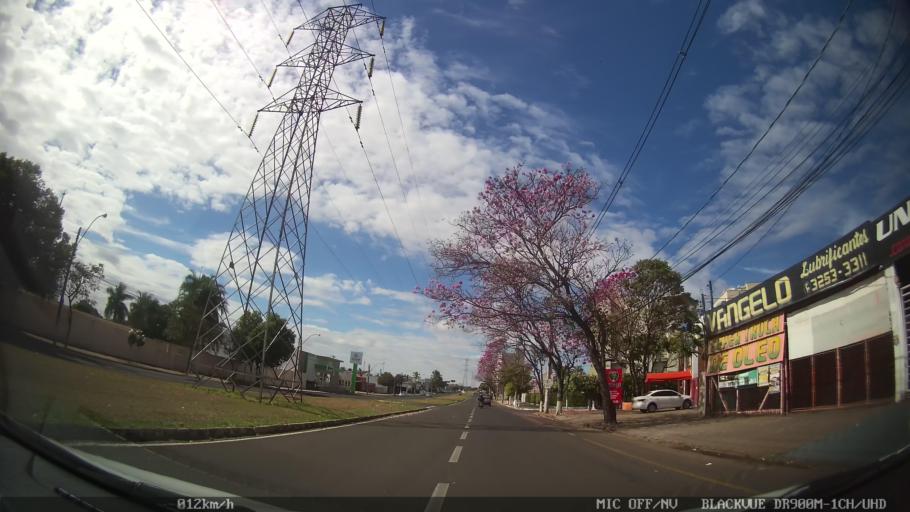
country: BR
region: Sao Paulo
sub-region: Bady Bassitt
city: Bady Bassitt
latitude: -20.8122
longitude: -49.5087
